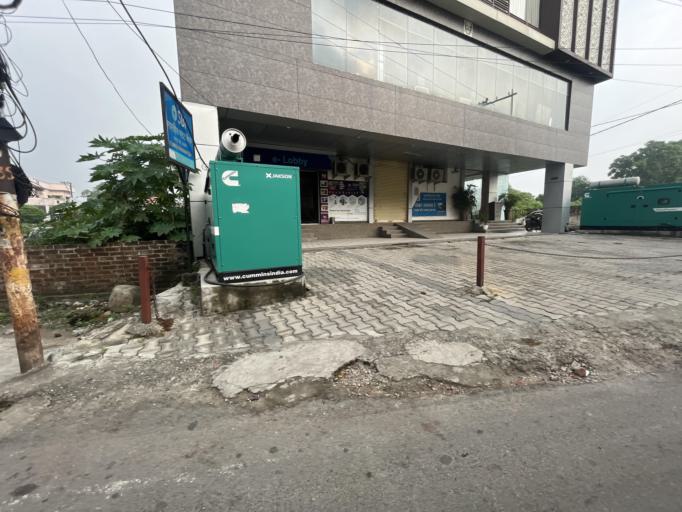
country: IN
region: Uttarakhand
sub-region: Naini Tal
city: Haldwani
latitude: 29.2104
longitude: 79.5245
